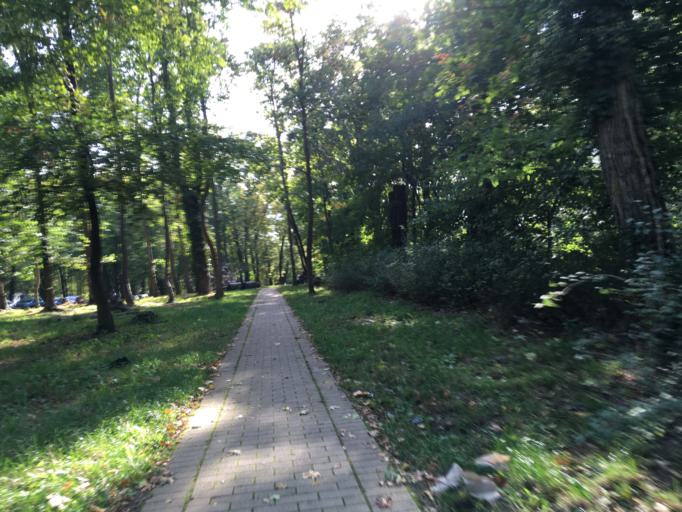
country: DE
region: Brandenburg
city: Hoppegarten
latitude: 52.5172
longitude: 13.6724
